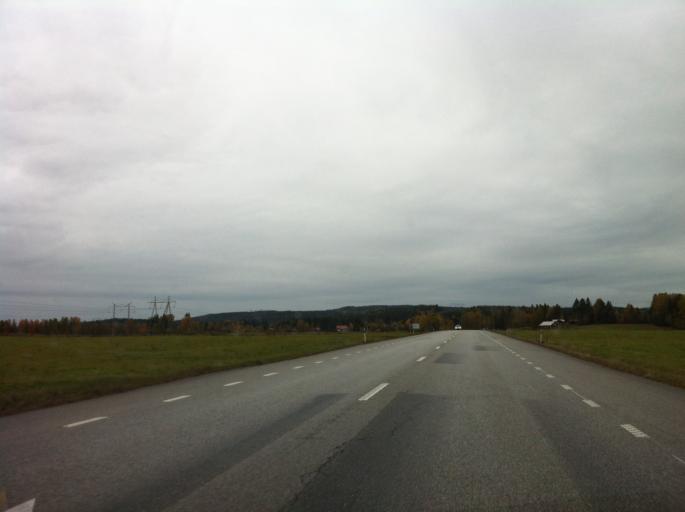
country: SE
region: OErebro
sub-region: Lindesbergs Kommun
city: Stora
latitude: 59.7928
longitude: 15.1532
